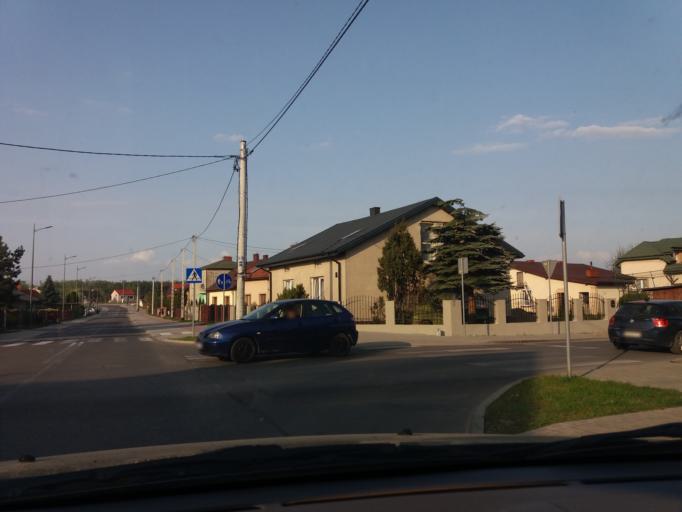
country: PL
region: Masovian Voivodeship
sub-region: Powiat mlawski
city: Mlawa
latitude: 53.1255
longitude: 20.3639
